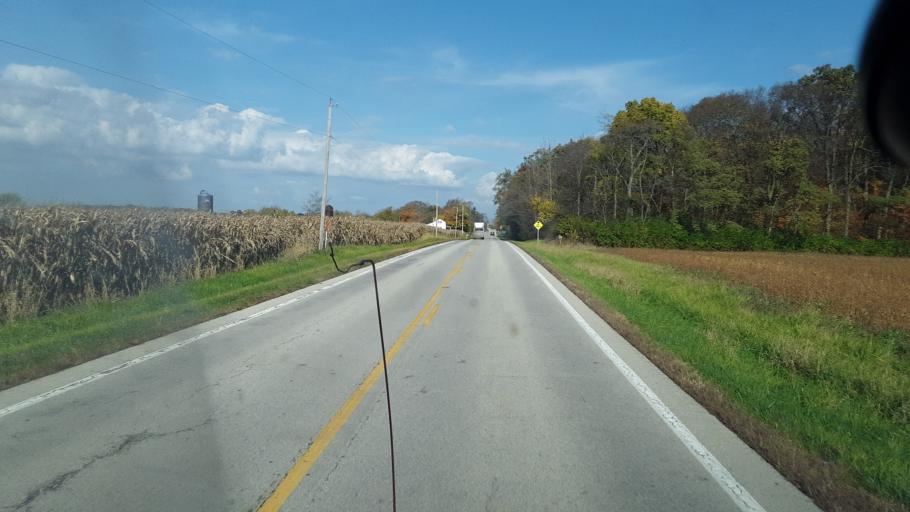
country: US
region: Ohio
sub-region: Clinton County
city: Sabina
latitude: 39.5326
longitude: -83.7031
